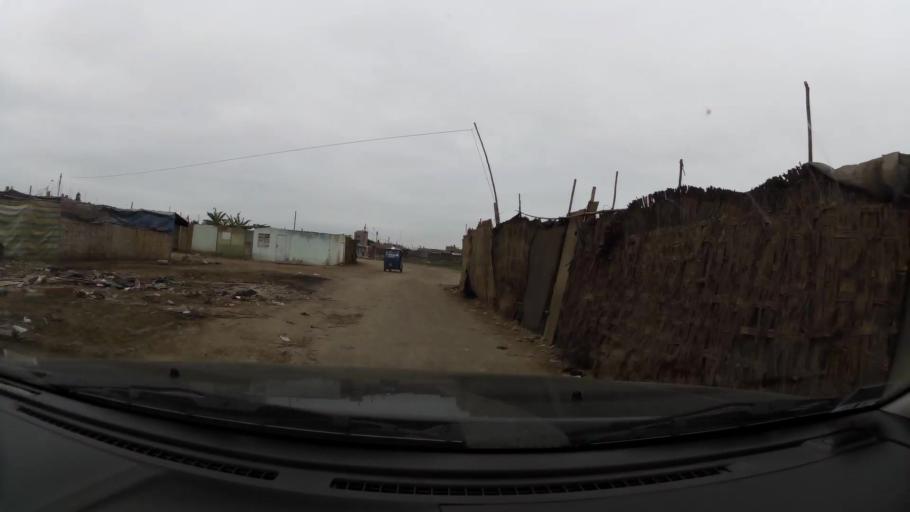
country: PE
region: Ica
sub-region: Provincia de Pisco
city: Pisco
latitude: -13.7145
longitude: -76.2126
